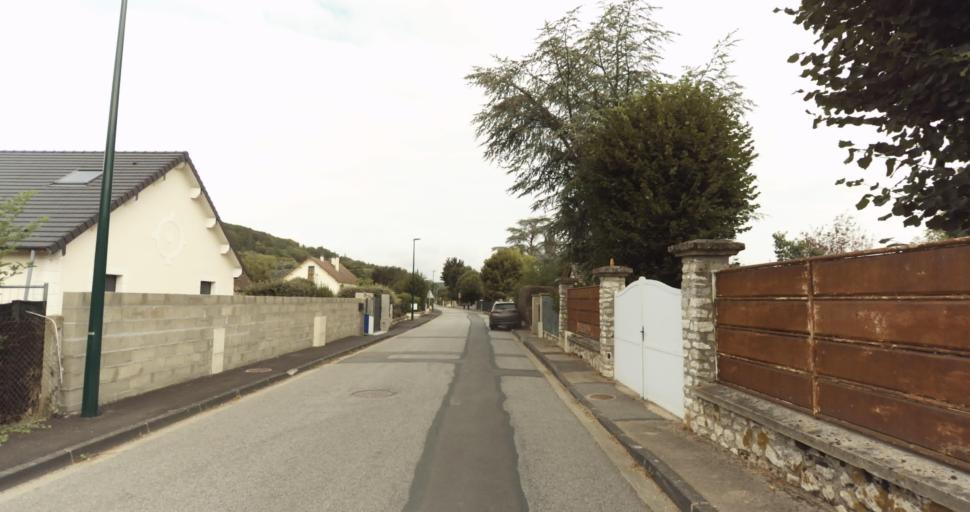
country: FR
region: Haute-Normandie
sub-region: Departement de l'Eure
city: Garennes-sur-Eure
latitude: 48.9164
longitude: 1.4316
